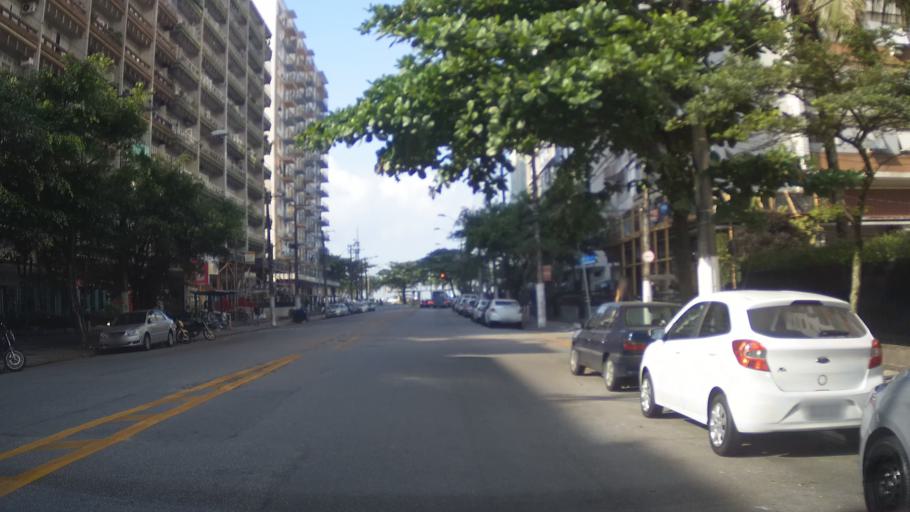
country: BR
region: Sao Paulo
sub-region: Santos
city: Santos
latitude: -23.9710
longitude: -46.3242
